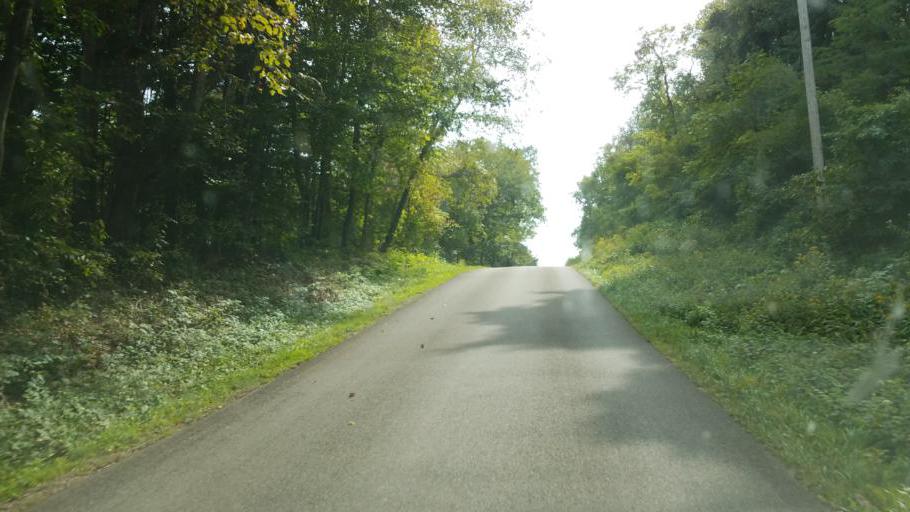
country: US
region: Ohio
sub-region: Knox County
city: Centerburg
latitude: 40.3671
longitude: -82.6057
